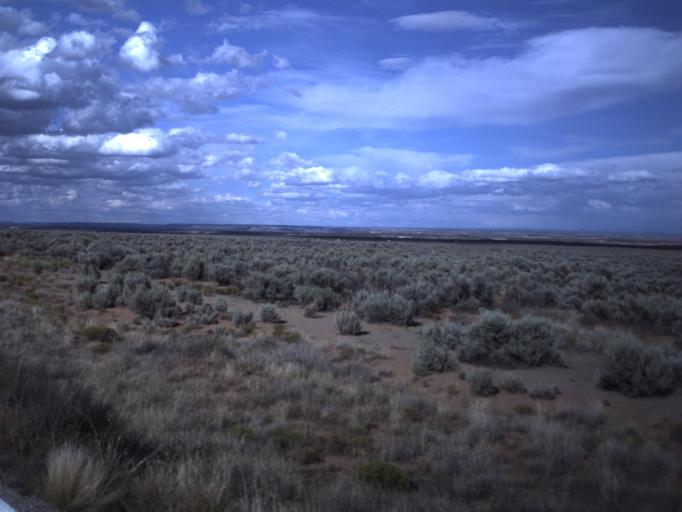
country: US
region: Utah
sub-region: San Juan County
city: Blanding
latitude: 37.3810
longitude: -109.3413
